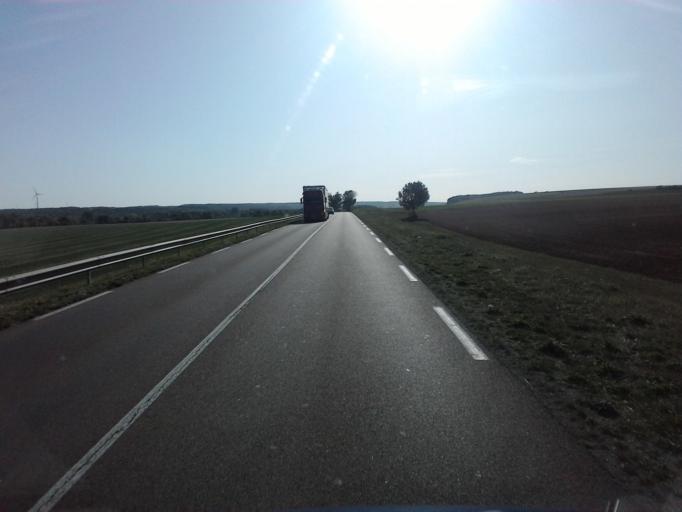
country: FR
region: Champagne-Ardenne
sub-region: Departement de l'Aube
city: Bar-sur-Seine
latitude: 48.1371
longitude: 4.3188
